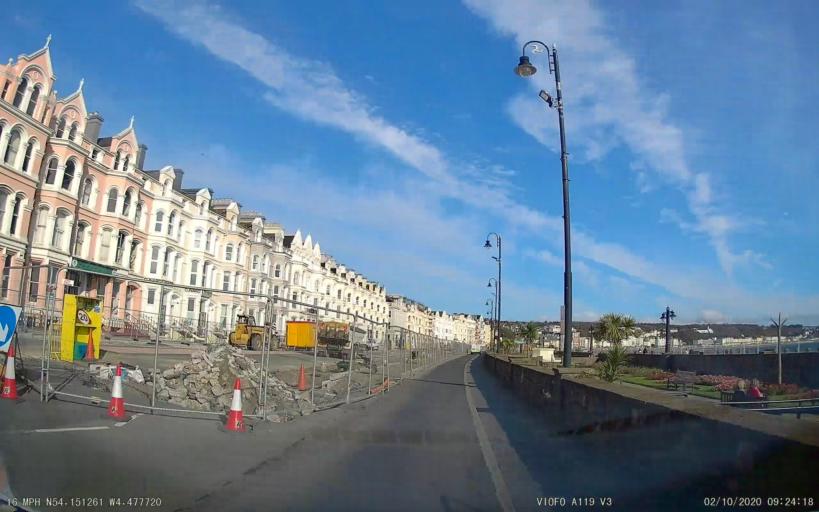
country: IM
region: Douglas
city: Douglas
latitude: 54.1517
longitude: -4.4784
